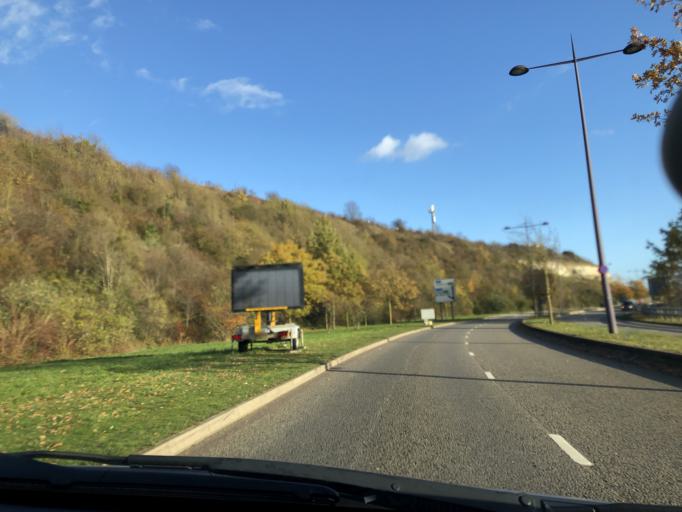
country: GB
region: England
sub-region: Kent
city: Stone
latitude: 51.4433
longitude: 0.2722
